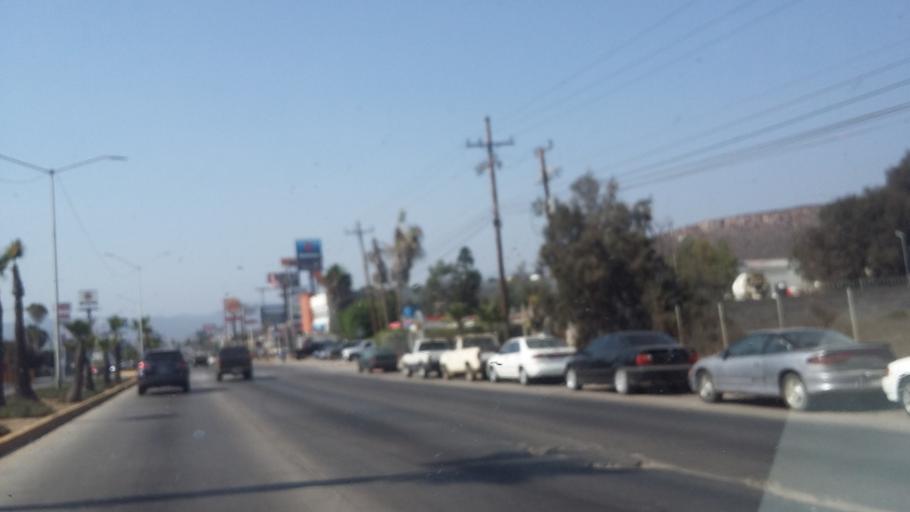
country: MX
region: Baja California
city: Ensenada
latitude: 31.8121
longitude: -116.5970
